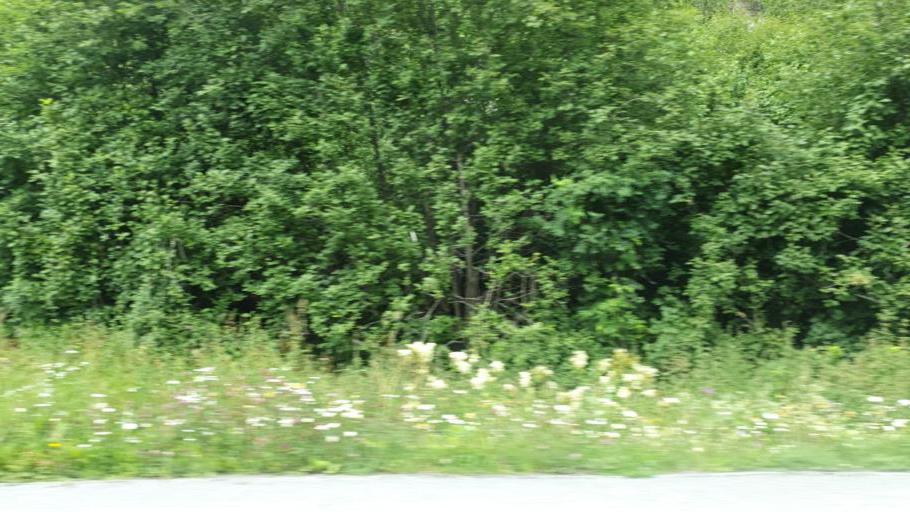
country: NO
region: Oppland
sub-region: Sel
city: Otta
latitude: 61.8424
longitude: 9.3895
